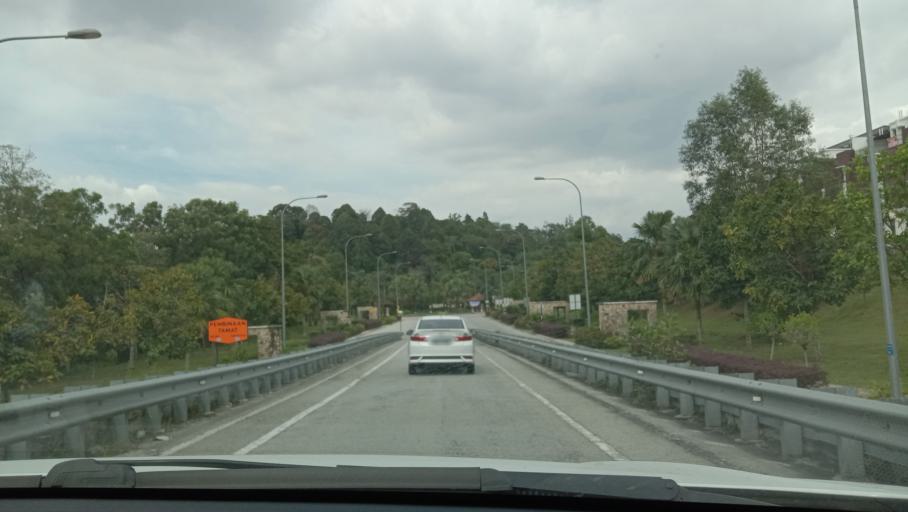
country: MY
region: Selangor
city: Kampung Baru Subang
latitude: 3.1342
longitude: 101.5010
